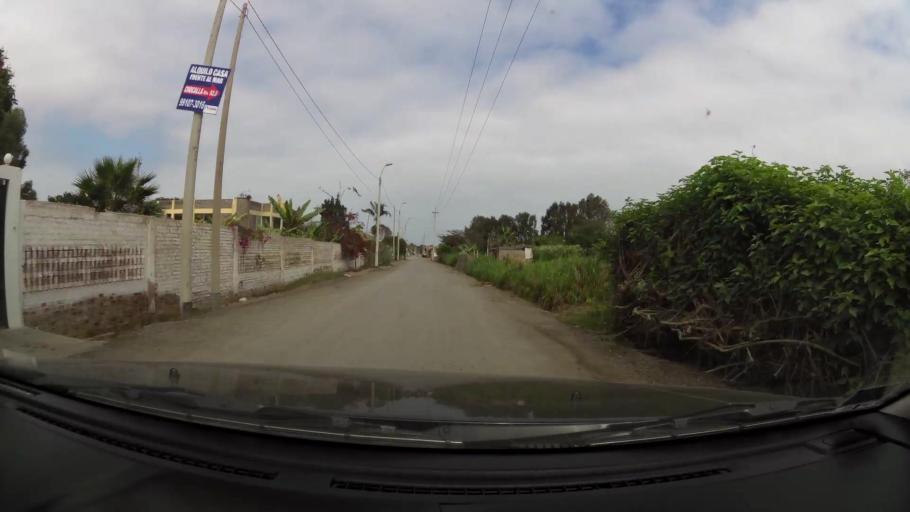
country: PE
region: Lima
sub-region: Provincia de Canete
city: Mala
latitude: -12.7261
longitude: -76.6180
